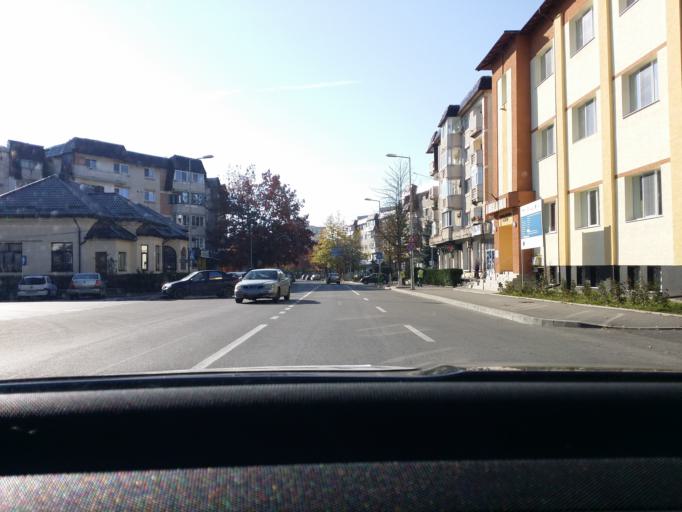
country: RO
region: Prahova
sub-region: Municipiul Campina
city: Campina
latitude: 45.1281
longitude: 25.7332
